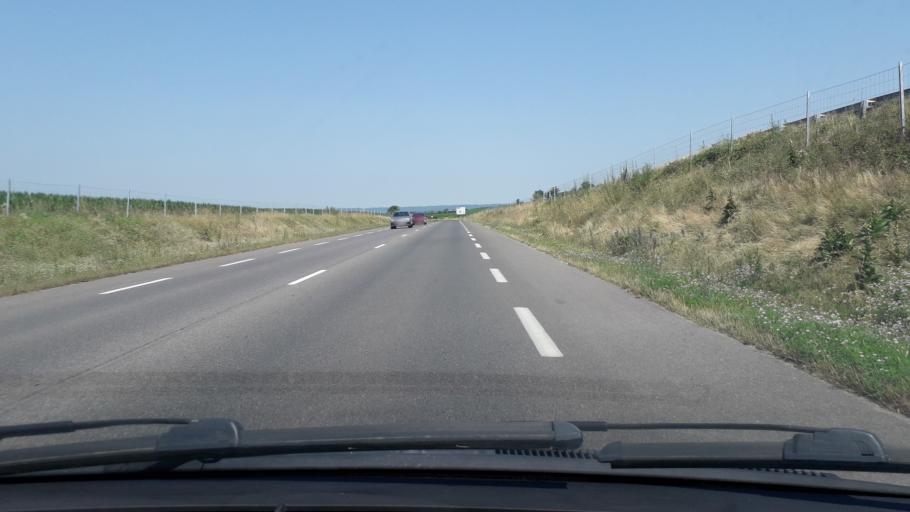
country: FR
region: Rhone-Alpes
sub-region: Departement de l'Isere
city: Janneyrias
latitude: 45.7643
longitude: 5.1225
